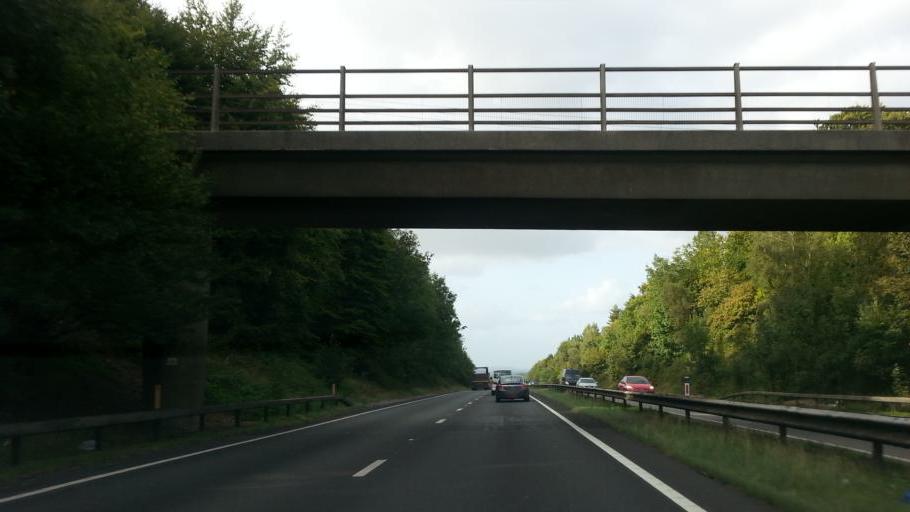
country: GB
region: England
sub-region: Hampshire
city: Kings Worthy
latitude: 51.1180
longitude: -1.3447
